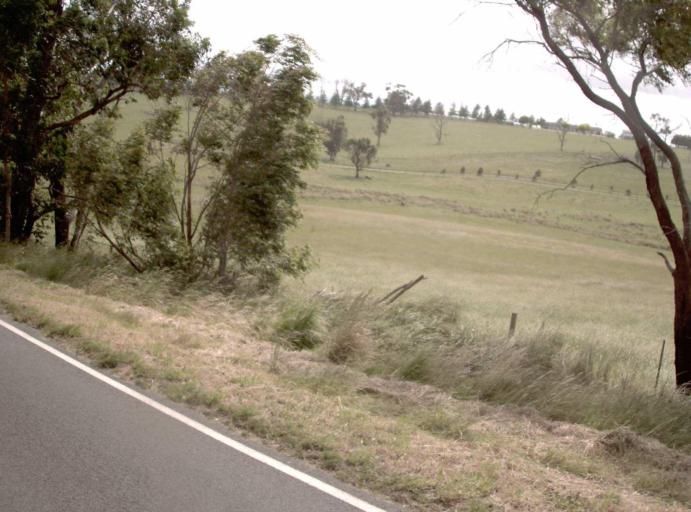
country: AU
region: Victoria
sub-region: Latrobe
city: Moe
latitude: -38.1408
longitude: 146.1471
